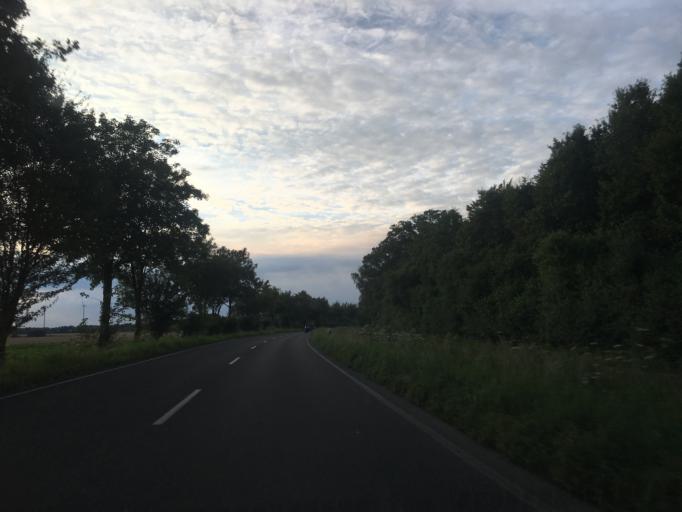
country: DE
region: North Rhine-Westphalia
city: Erkelenz
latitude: 51.0489
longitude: 6.2790
